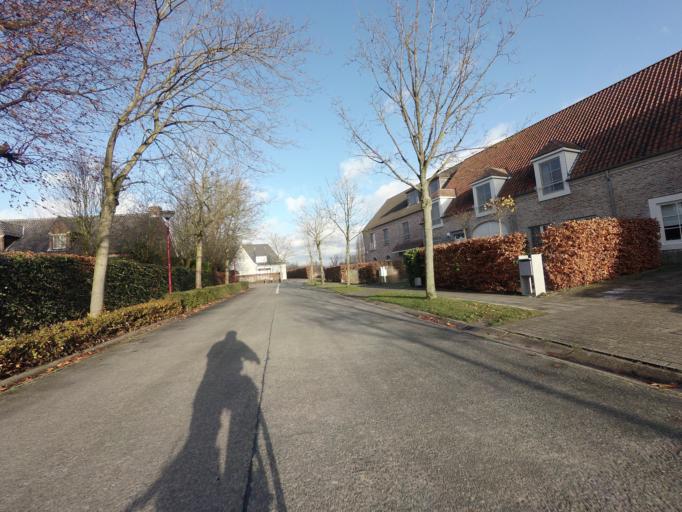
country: BE
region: Flanders
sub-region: Provincie Antwerpen
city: Lint
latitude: 51.1276
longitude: 4.5015
